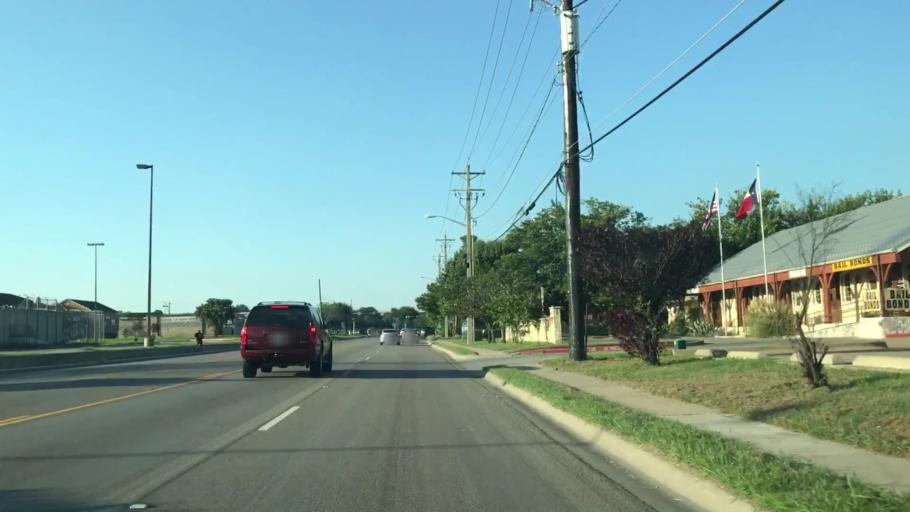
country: US
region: Texas
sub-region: Denton County
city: Denton
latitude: 33.2135
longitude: -97.1120
